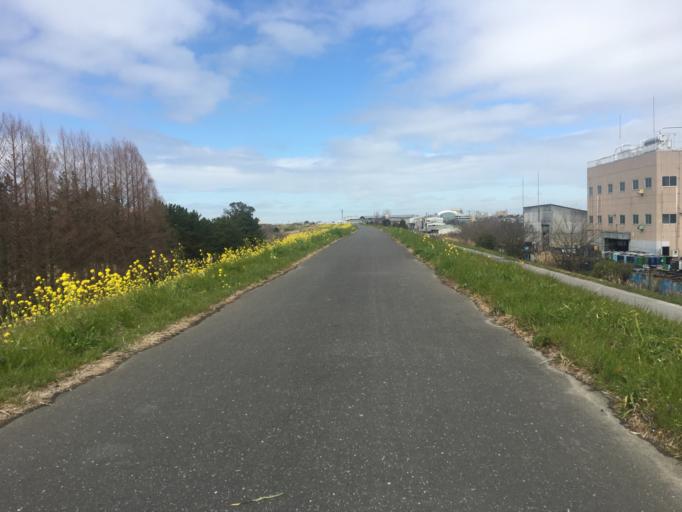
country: JP
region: Saitama
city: Shiki
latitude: 35.8466
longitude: 139.6141
